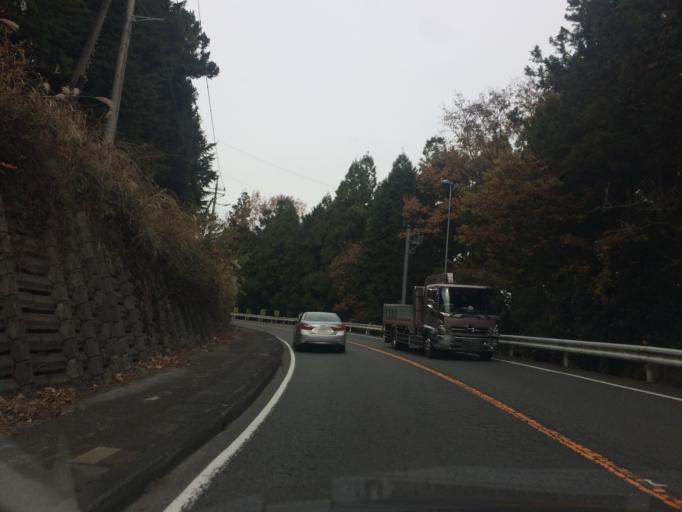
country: JP
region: Shizuoka
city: Fujinomiya
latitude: 35.3119
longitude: 138.4421
